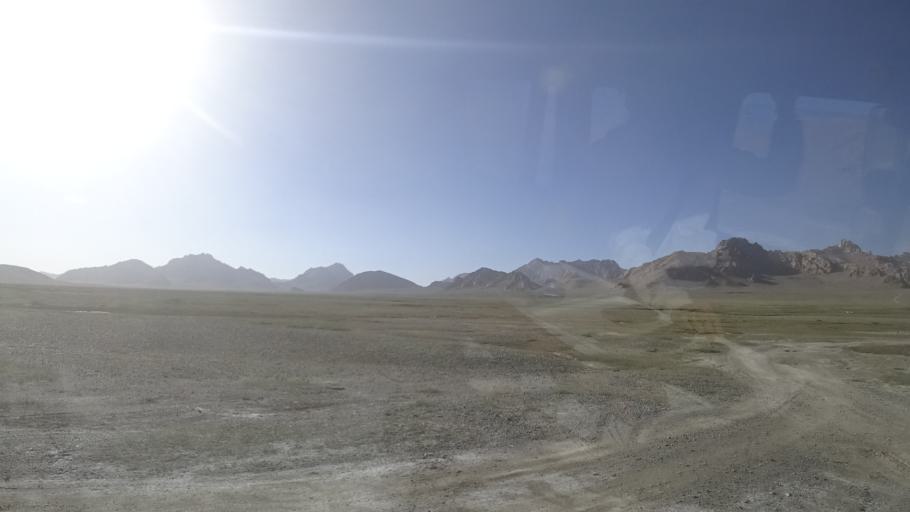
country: TJ
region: Gorno-Badakhshan
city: Murghob
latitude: 37.6608
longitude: 74.1696
